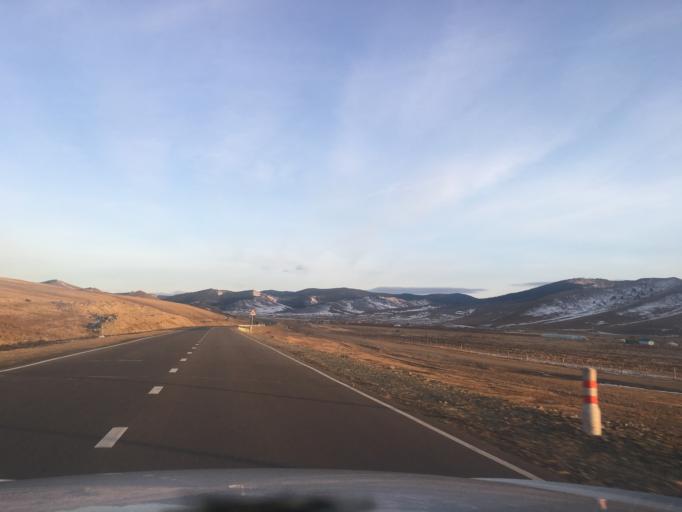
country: MN
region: Central Aimak
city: Mandal
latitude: 48.1111
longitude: 106.7098
